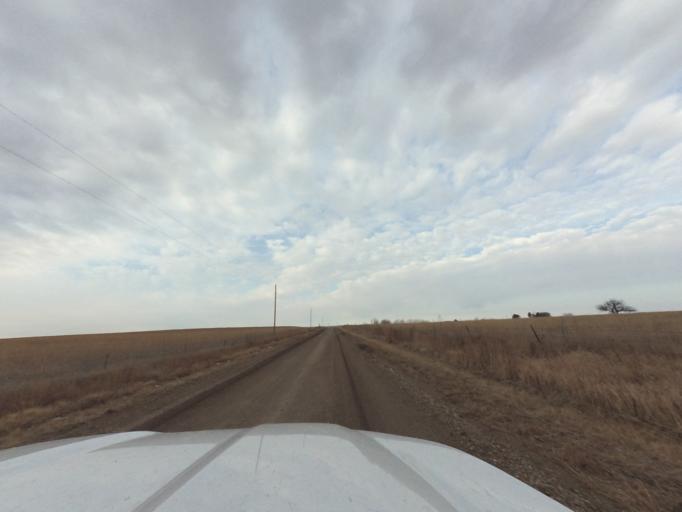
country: US
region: Kansas
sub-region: Chase County
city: Cottonwood Falls
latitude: 38.4492
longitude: -96.3792
